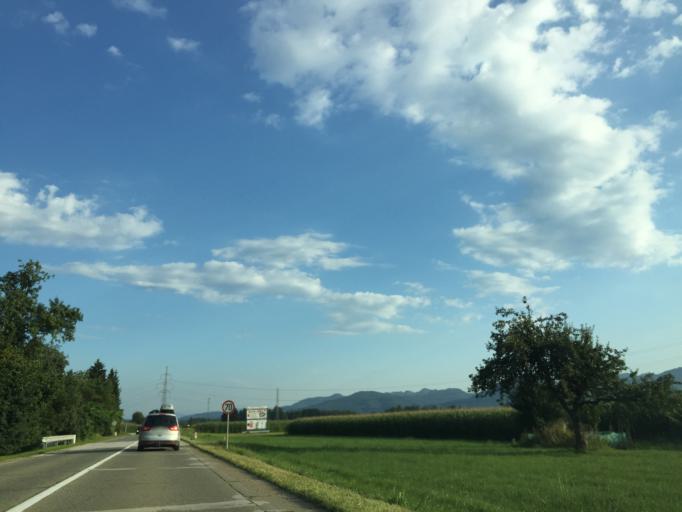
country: SI
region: Sencur
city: Hrastje
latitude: 46.1909
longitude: 14.3765
